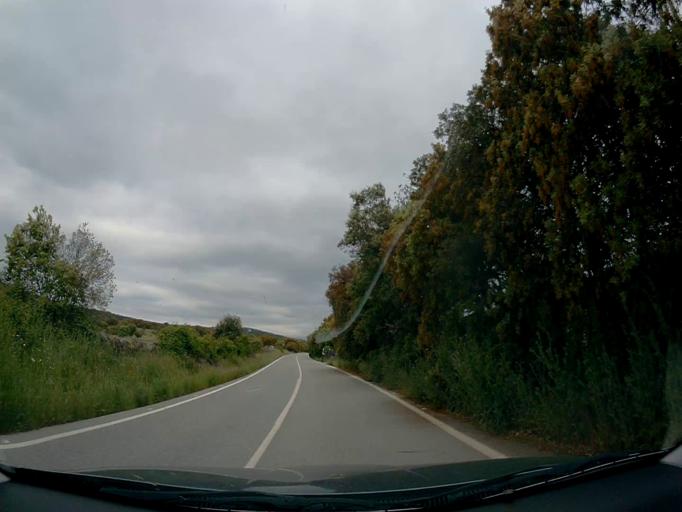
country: ES
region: Madrid
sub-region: Provincia de Madrid
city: Navalagamella
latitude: 40.4514
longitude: -4.1129
